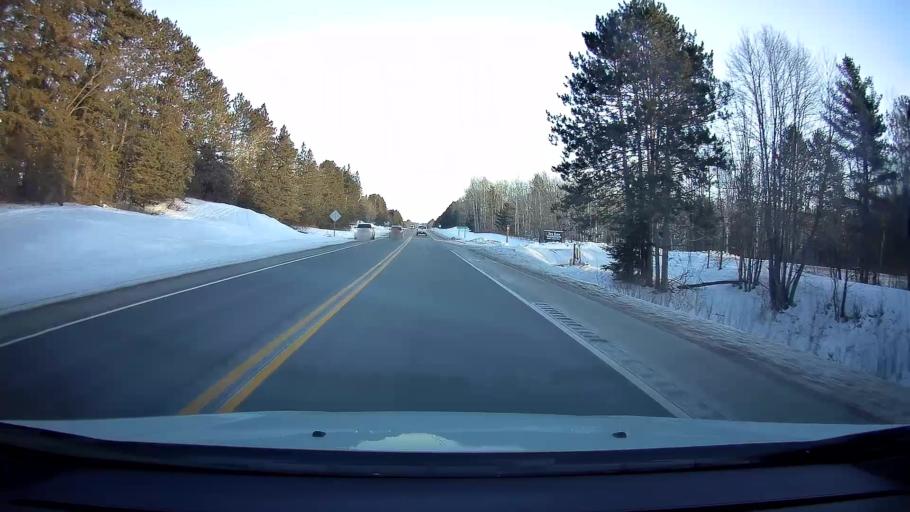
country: US
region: Wisconsin
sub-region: Washburn County
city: Shell Lake
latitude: 45.7508
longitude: -91.9168
